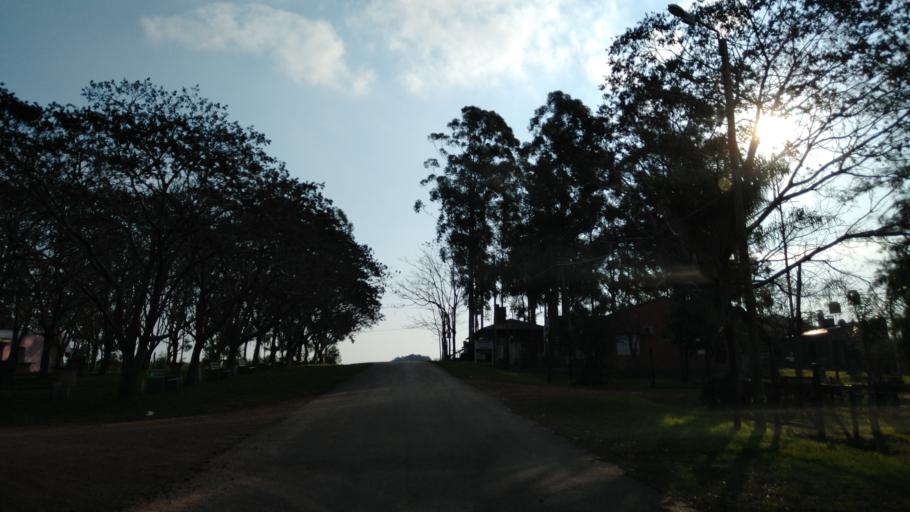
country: AR
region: Entre Rios
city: Santa Ana
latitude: -30.9128
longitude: -57.9257
